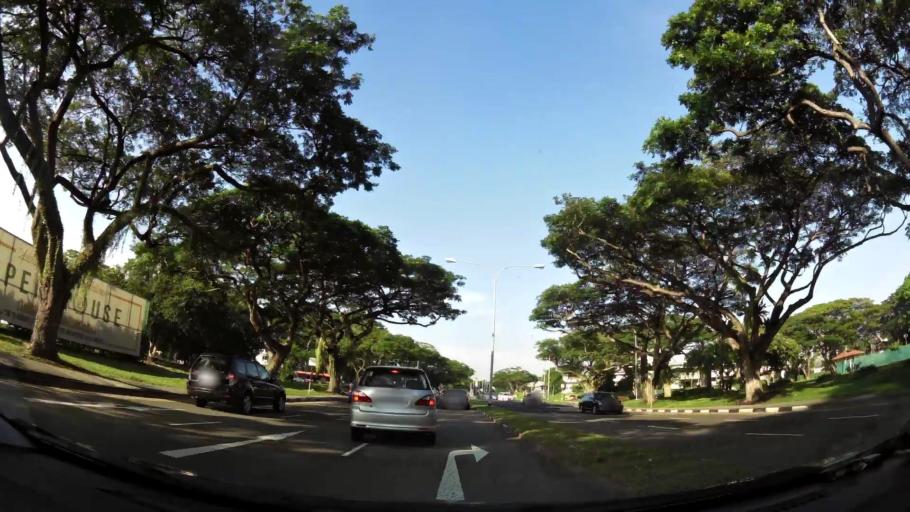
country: SG
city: Singapore
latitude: 1.3190
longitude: 103.9336
